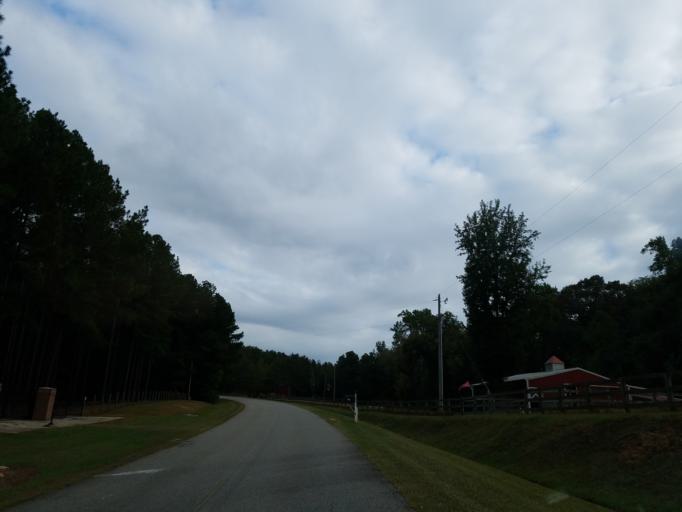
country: US
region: Georgia
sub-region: Lamar County
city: Barnesville
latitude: 33.1653
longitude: -84.0838
